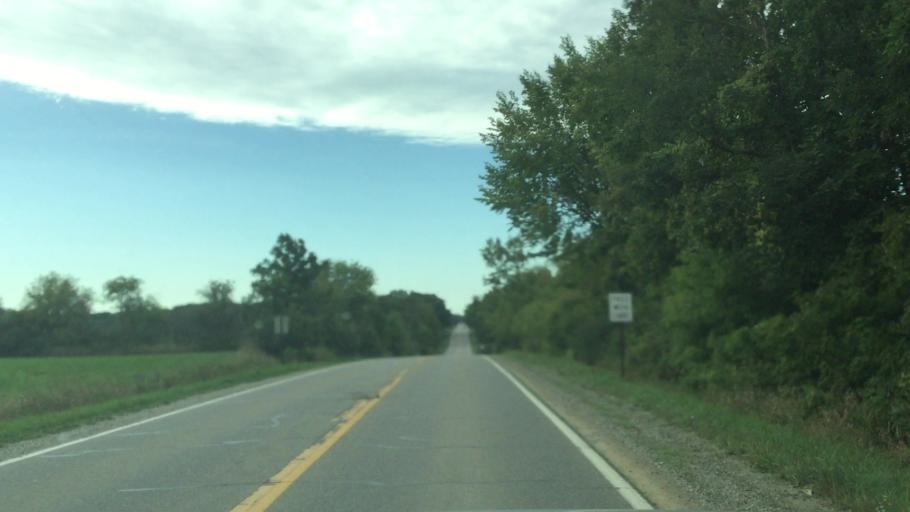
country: US
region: Michigan
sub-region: Livingston County
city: Howell
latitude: 42.6410
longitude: -83.8759
